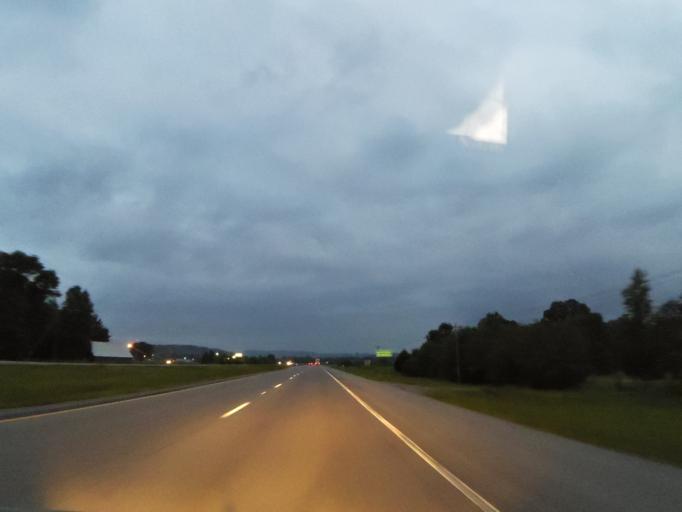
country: US
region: Alabama
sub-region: Madison County
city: New Hope
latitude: 34.6199
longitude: -86.2991
